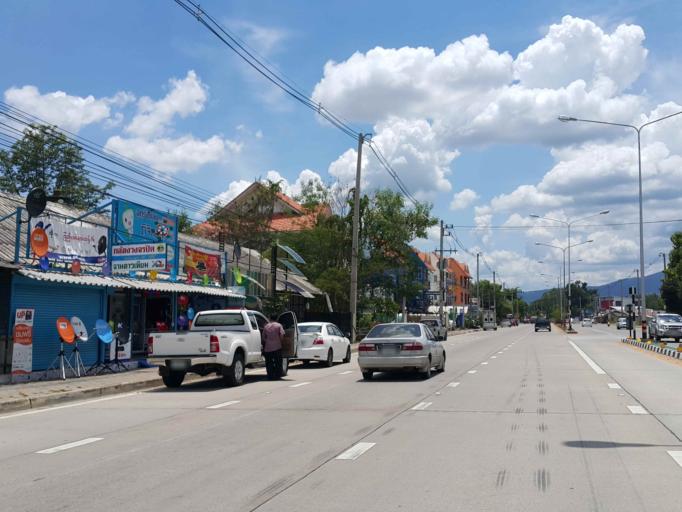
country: TH
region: Chiang Mai
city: Saraphi
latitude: 18.7427
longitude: 98.9993
